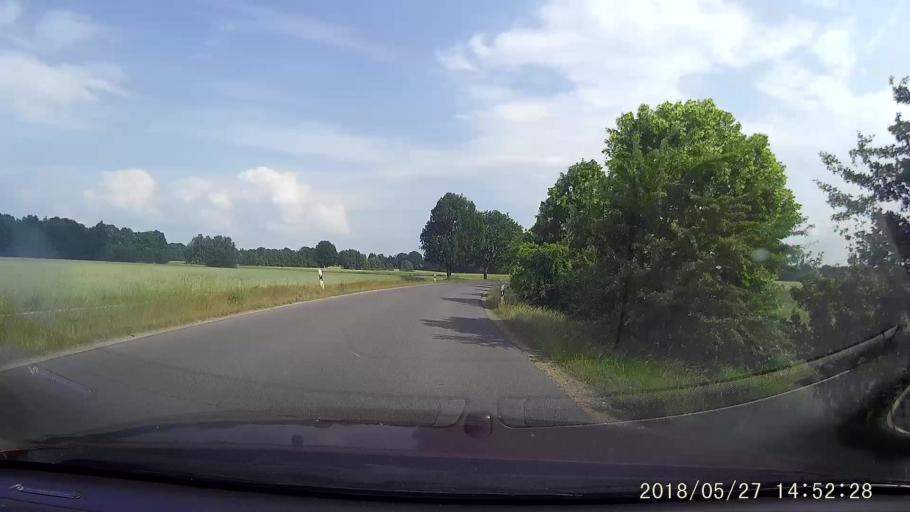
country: DE
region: Saxony
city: Klitten
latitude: 51.3567
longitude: 14.5834
